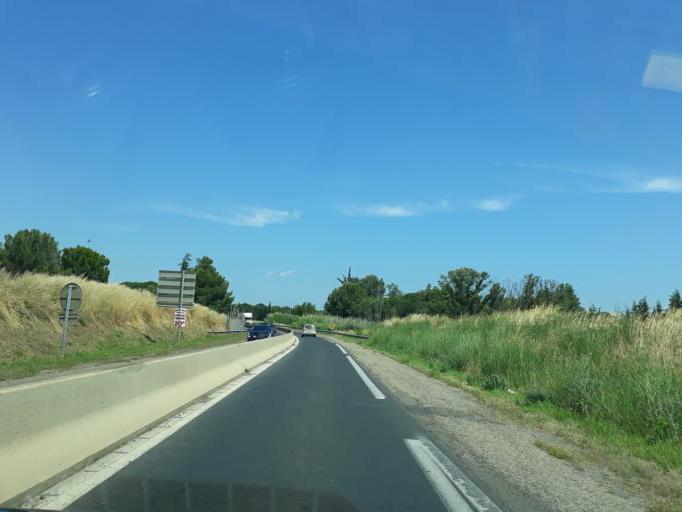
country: FR
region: Languedoc-Roussillon
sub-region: Departement de l'Herault
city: Vias
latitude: 43.3068
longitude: 3.4234
